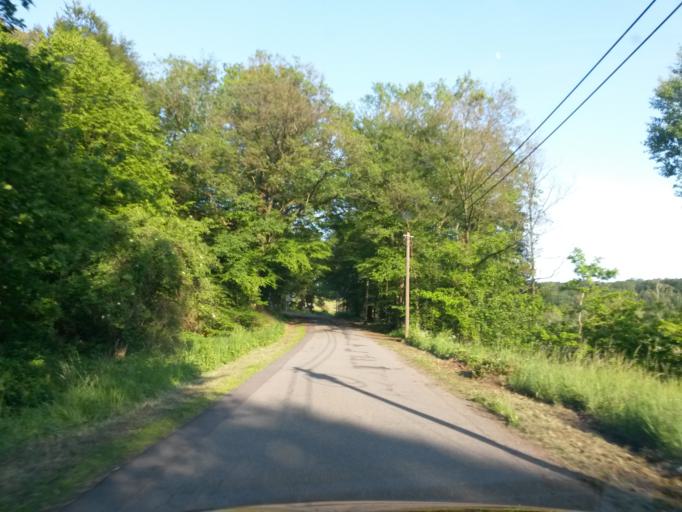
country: DE
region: North Rhine-Westphalia
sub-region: Regierungsbezirk Koln
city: Much
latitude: 50.8945
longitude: 7.3595
